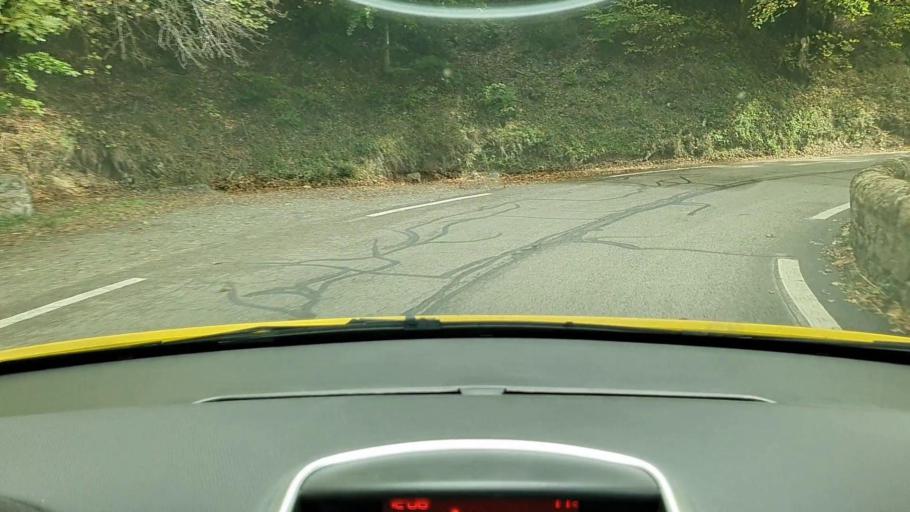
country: FR
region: Languedoc-Roussillon
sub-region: Departement de la Lozere
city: Meyrueis
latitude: 44.1244
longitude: 3.4752
